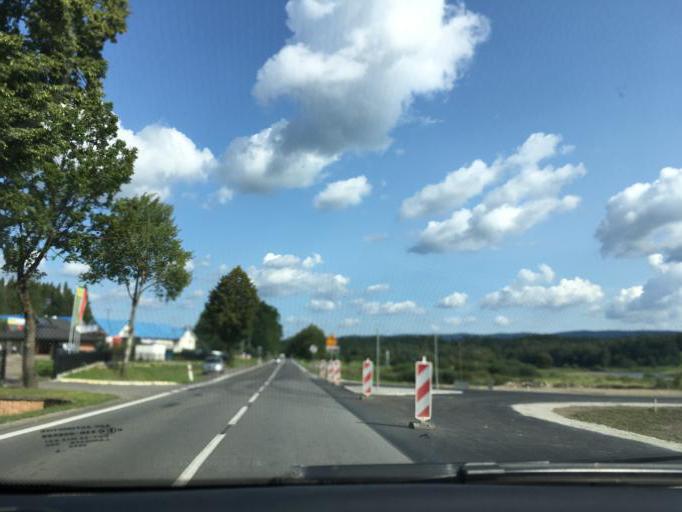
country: PL
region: Subcarpathian Voivodeship
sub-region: Powiat leski
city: Lesko
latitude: 49.4819
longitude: 22.3234
